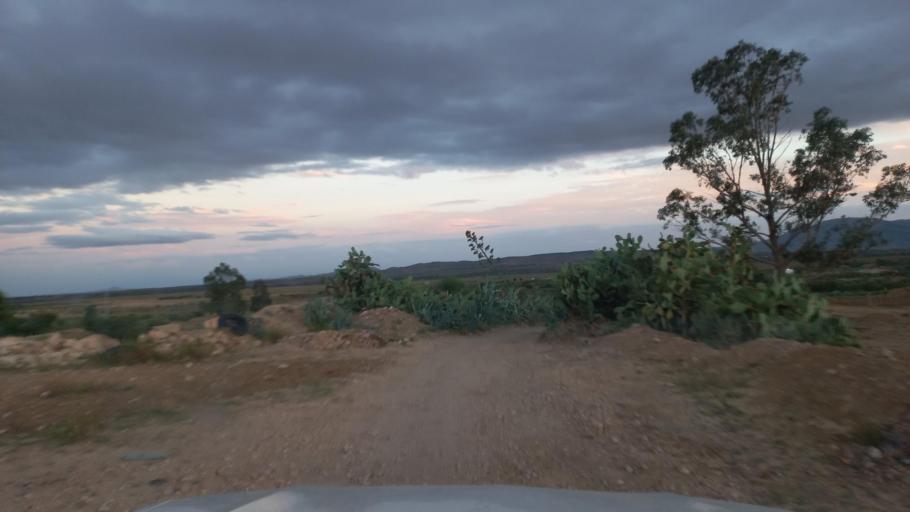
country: TN
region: Al Qasrayn
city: Kasserine
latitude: 35.2563
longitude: 8.9355
